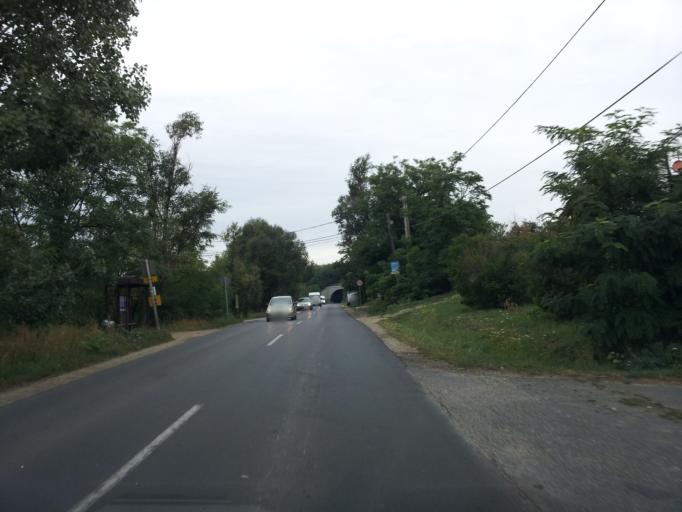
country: HU
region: Pest
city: Tarnok
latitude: 47.3893
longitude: 18.8541
